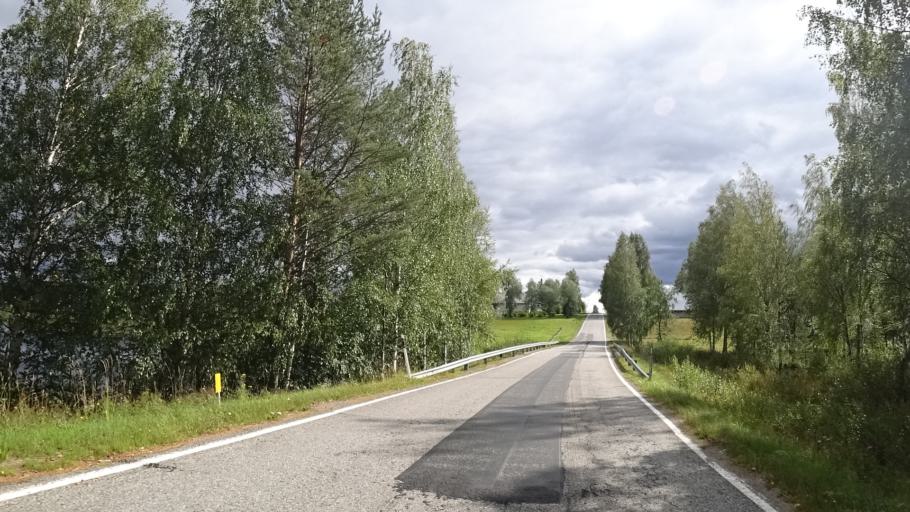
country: FI
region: North Karelia
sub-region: Joensuu
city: Ilomantsi
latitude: 62.4522
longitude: 31.1147
